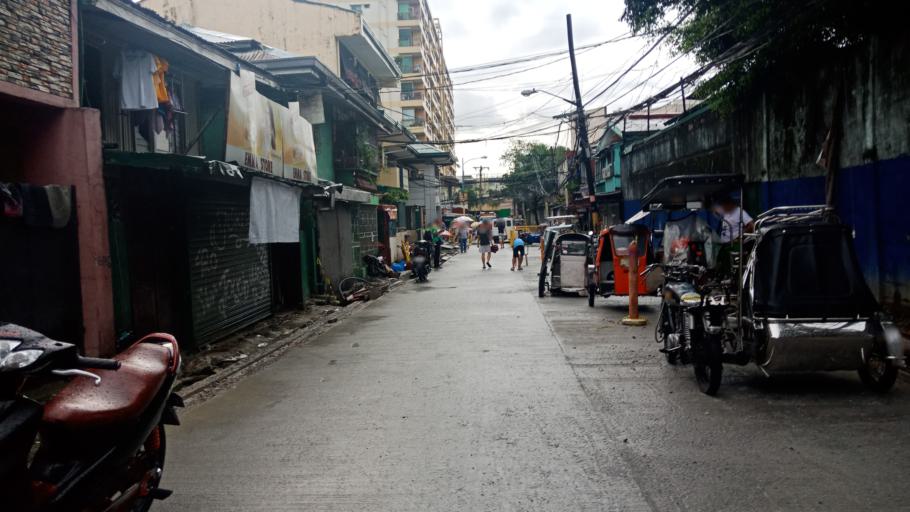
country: PH
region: Metro Manila
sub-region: San Juan
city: San Juan
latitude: 14.5910
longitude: 121.0307
